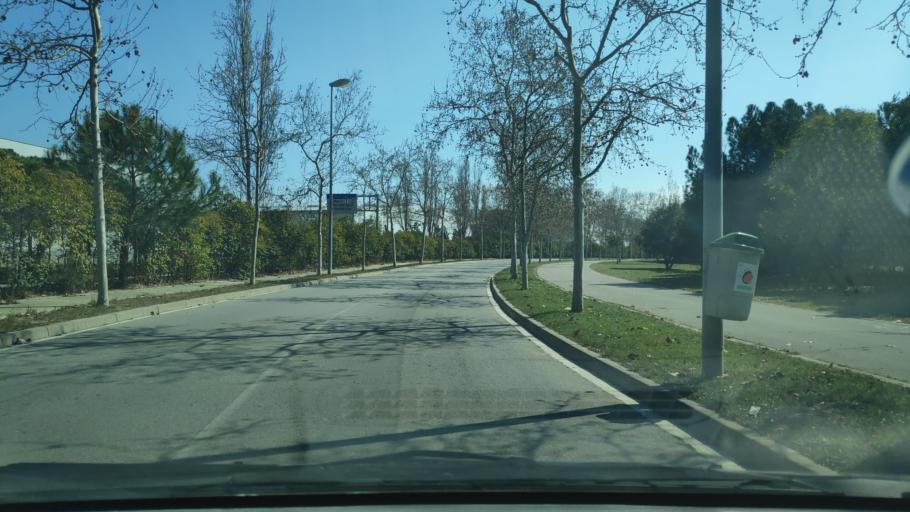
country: ES
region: Catalonia
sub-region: Provincia de Barcelona
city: Santa Perpetua de Mogoda
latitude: 41.5358
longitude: 2.1869
